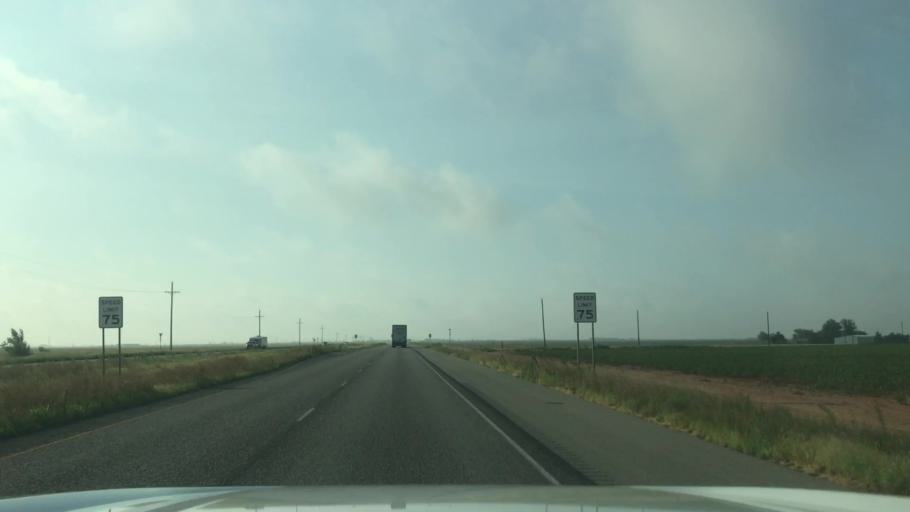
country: US
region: Texas
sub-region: Garza County
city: Post
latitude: 33.2552
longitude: -101.4703
